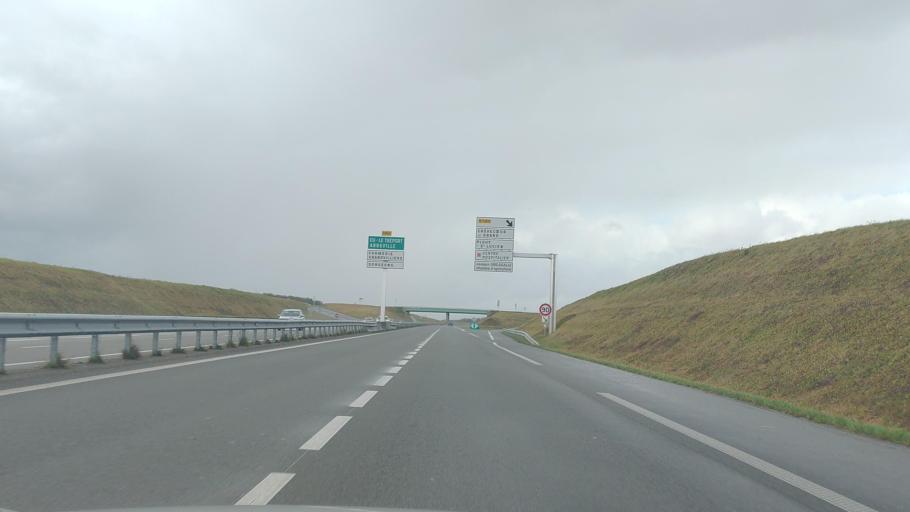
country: FR
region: Picardie
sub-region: Departement de l'Oise
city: Tille
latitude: 49.4651
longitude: 2.0809
